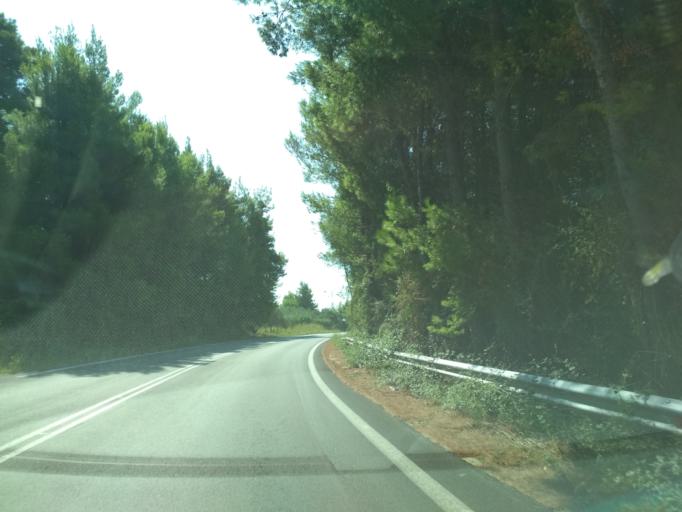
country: GR
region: Central Greece
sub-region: Nomos Evvoias
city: Roviai
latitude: 38.8240
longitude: 23.2276
